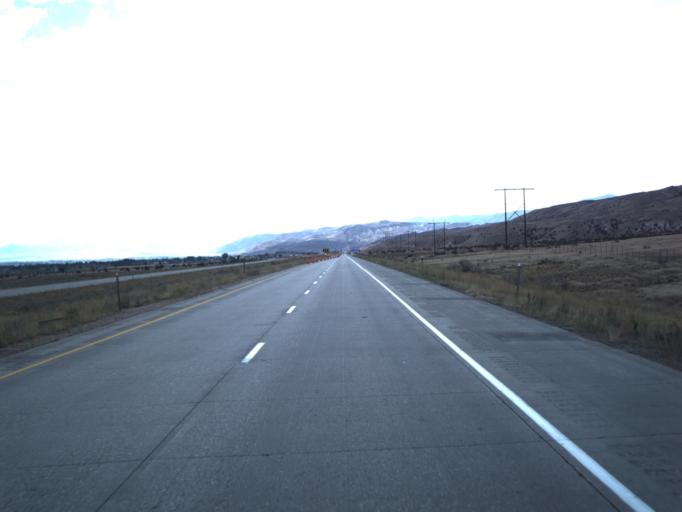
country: US
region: Utah
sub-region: Sevier County
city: Richfield
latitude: 38.8177
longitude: -112.0498
